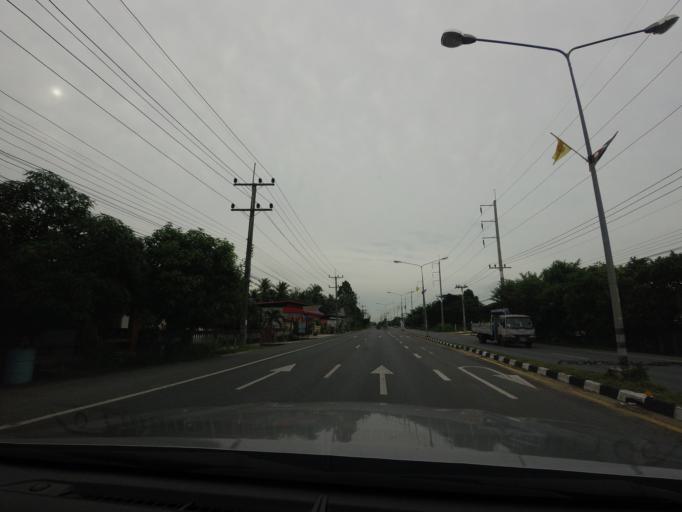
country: TH
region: Songkhla
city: Sathing Phra
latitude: 7.4889
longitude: 100.4342
